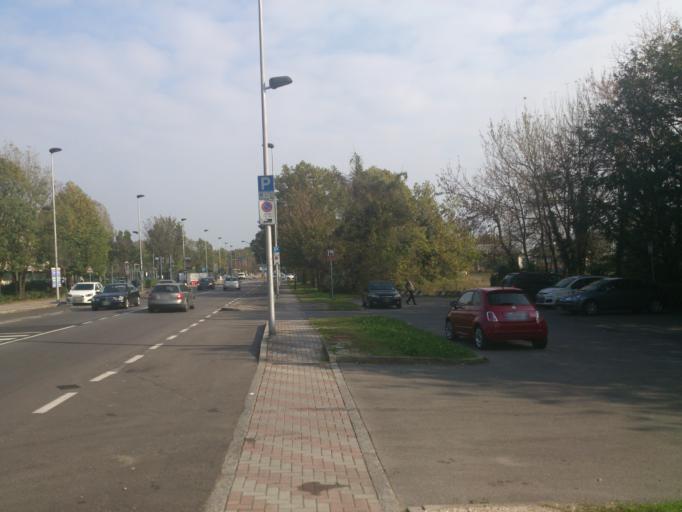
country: IT
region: Lombardy
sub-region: Citta metropolitana di Milano
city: San Donato Milanese
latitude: 45.4138
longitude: 9.2772
